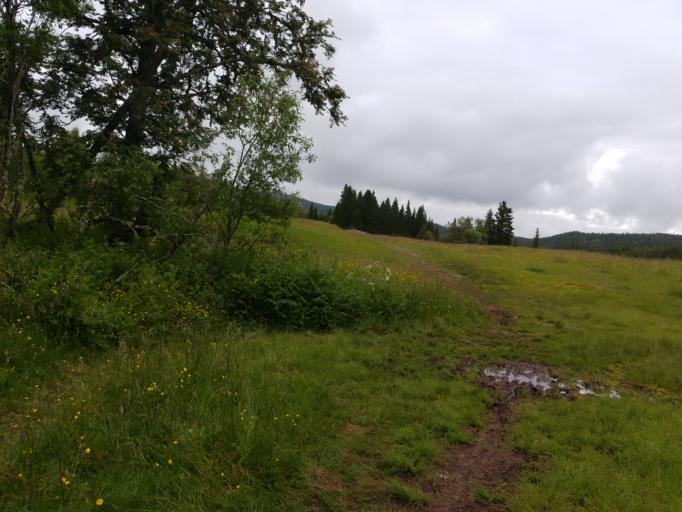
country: NO
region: Sor-Trondelag
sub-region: Melhus
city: Melhus
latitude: 63.3855
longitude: 10.2943
